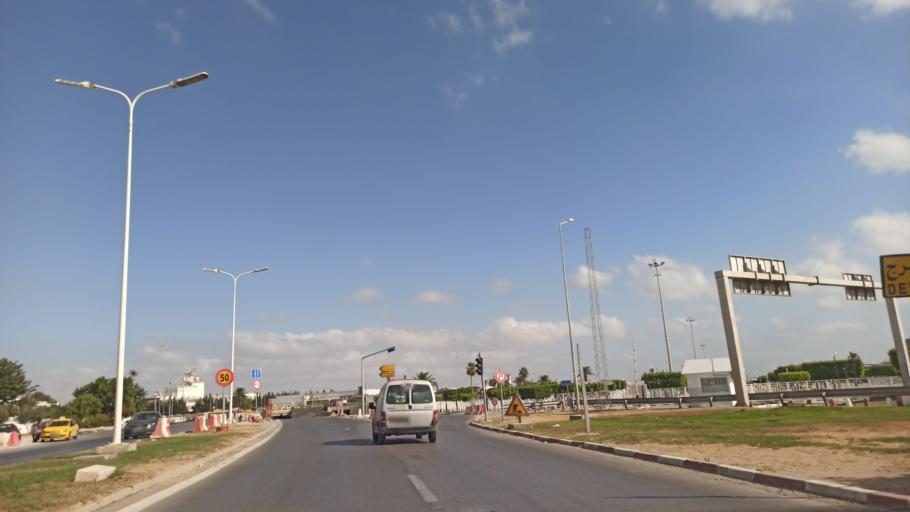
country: TN
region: Ariana
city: Ariana
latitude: 36.8459
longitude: 10.2148
